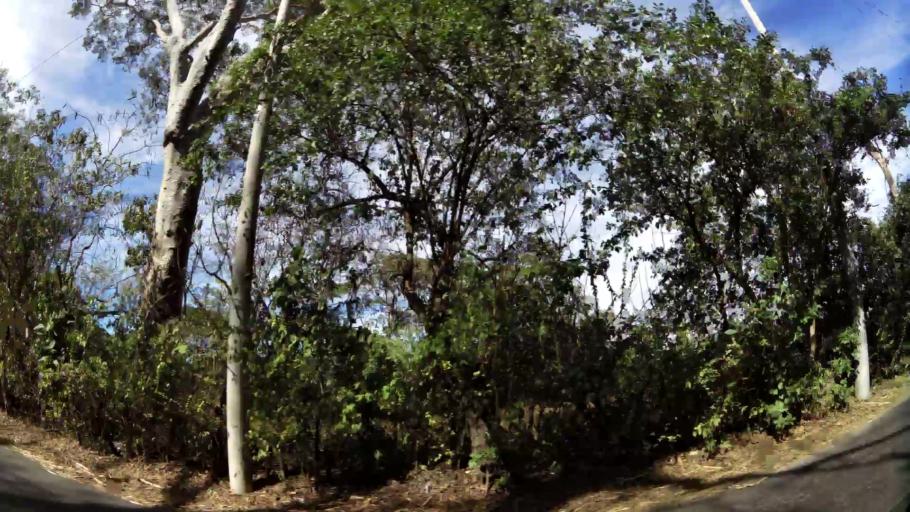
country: SV
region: San Salvador
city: Aguilares
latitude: 13.9631
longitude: -89.1717
